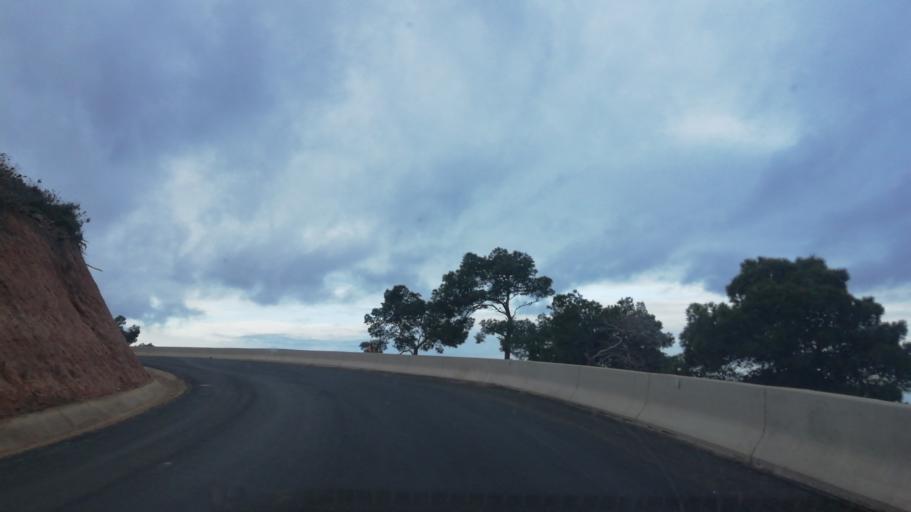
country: DZ
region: Oran
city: Bir el Djir
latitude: 35.7617
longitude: -0.5301
